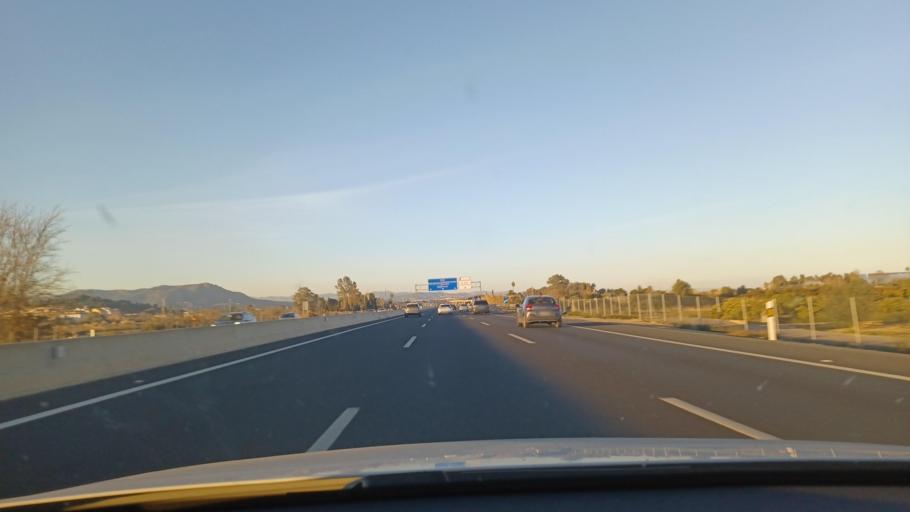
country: ES
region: Valencia
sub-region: Provincia de Valencia
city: Puig
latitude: 39.5810
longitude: -0.2944
